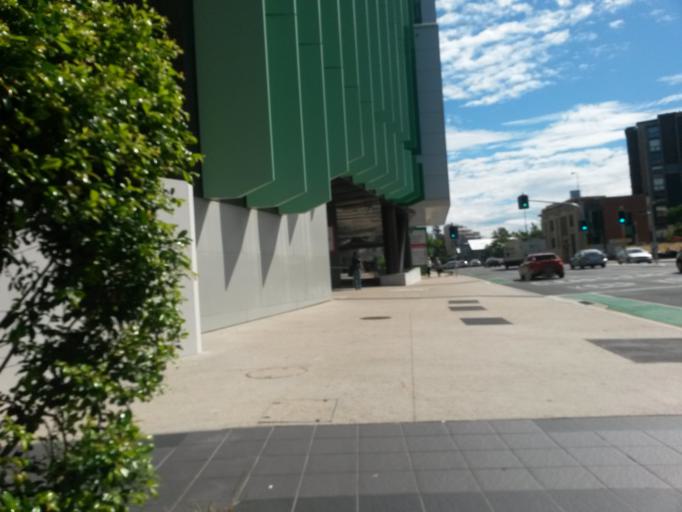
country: AU
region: Queensland
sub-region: Brisbane
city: South Brisbane
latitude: -27.4844
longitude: 153.0274
